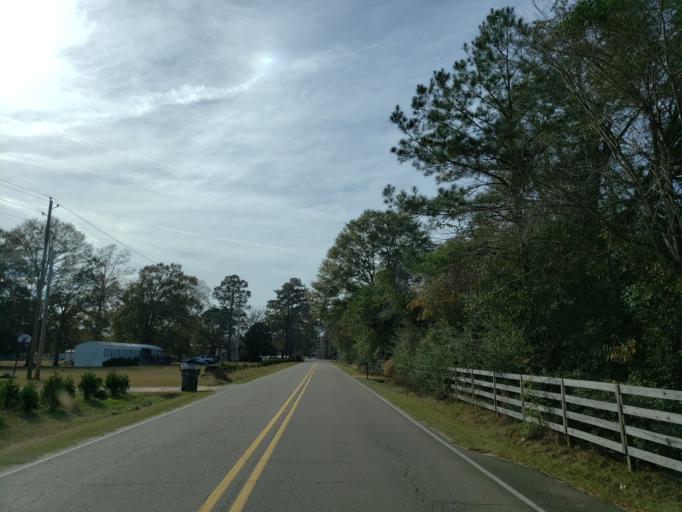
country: US
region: Mississippi
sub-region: Forrest County
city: Rawls Springs
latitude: 31.3921
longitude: -89.3742
